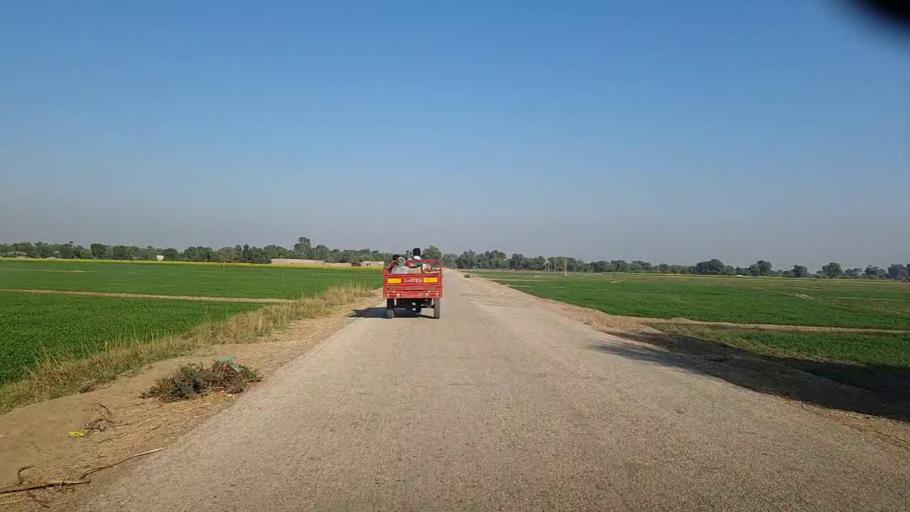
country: PK
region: Sindh
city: Darya Khan Marri
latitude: 26.6989
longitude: 68.3560
